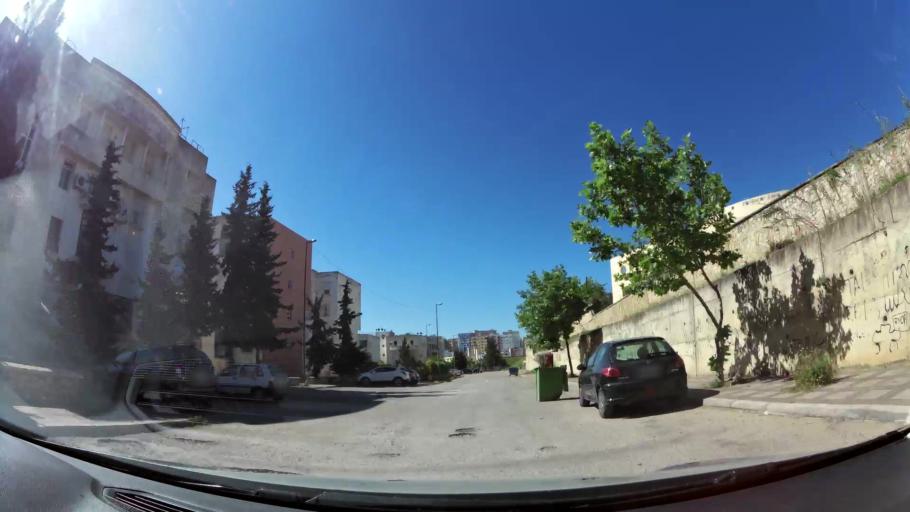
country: MA
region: Meknes-Tafilalet
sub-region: Meknes
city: Meknes
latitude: 33.9072
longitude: -5.5439
